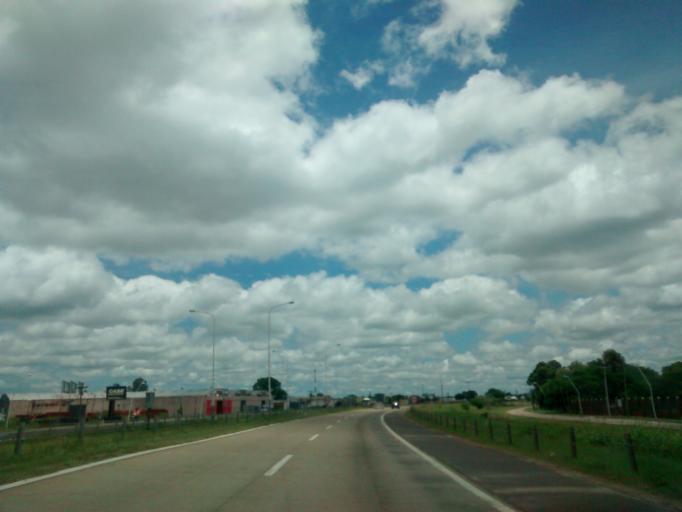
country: AR
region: Chaco
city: Fontana
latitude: -27.4124
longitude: -58.9964
